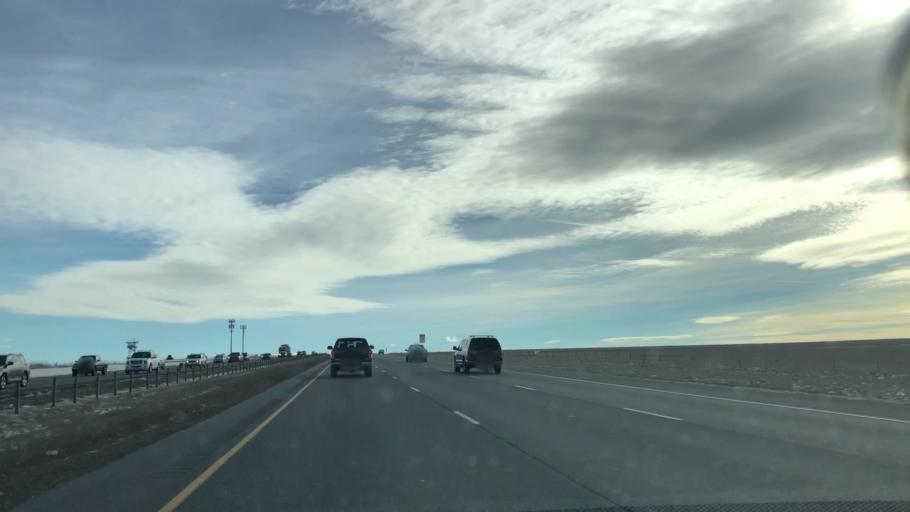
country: US
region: Colorado
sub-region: Weld County
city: Mead
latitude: 40.2759
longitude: -104.9806
